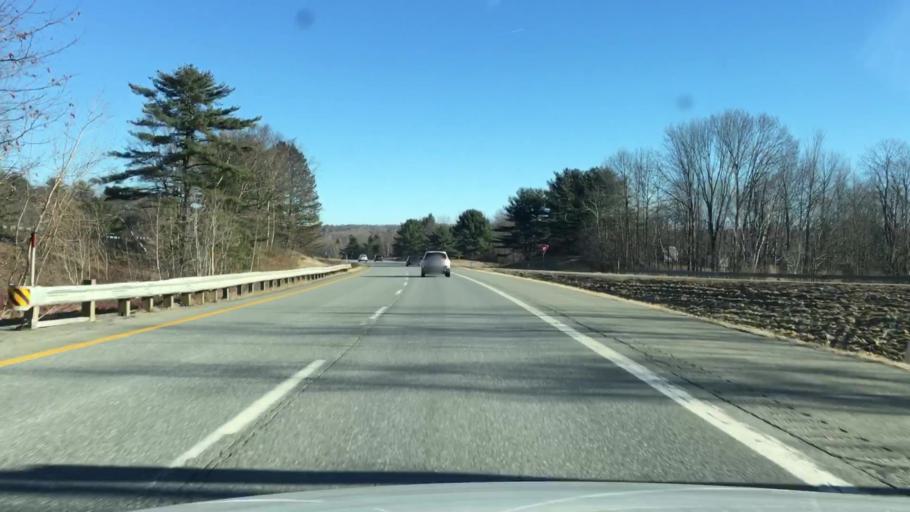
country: US
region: Maine
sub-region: Penobscot County
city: Hermon
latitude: 44.7584
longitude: -68.9720
